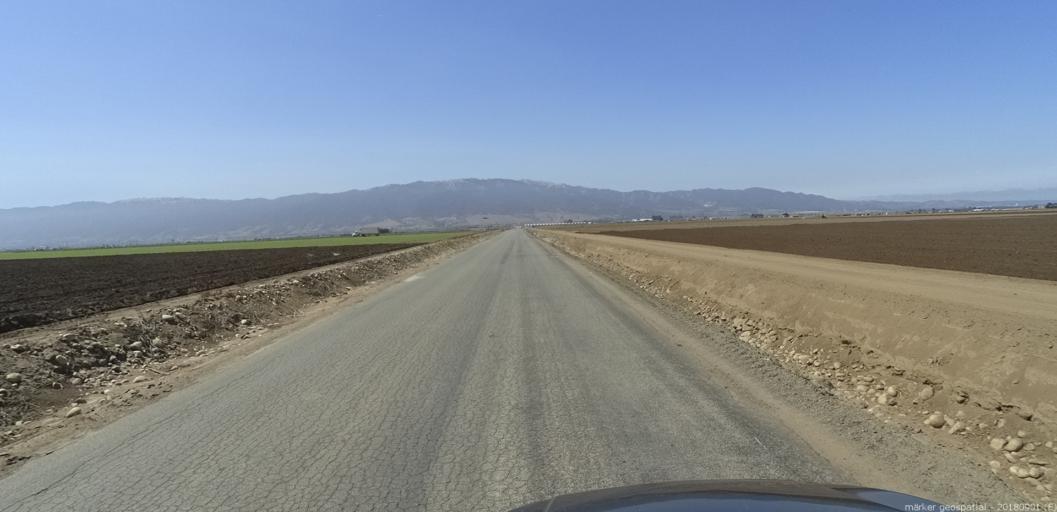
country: US
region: California
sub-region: Monterey County
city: Chualar
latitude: 36.6030
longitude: -121.5160
